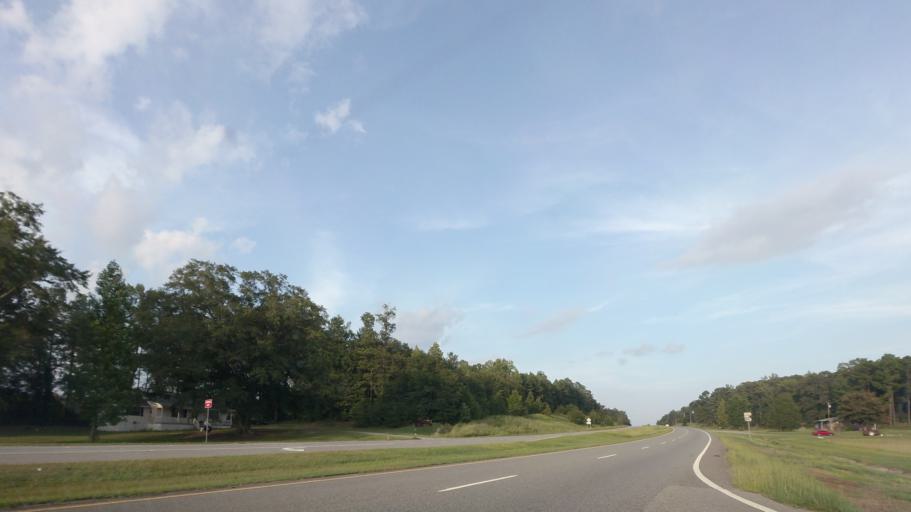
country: US
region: Georgia
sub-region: Wilkinson County
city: Gordon
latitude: 32.8480
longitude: -83.4219
